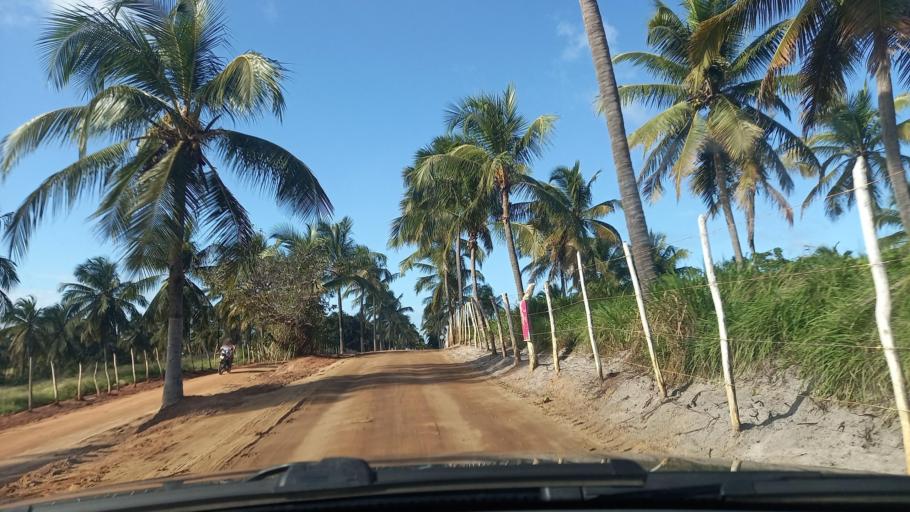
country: BR
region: Alagoas
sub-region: Marechal Deodoro
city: Marechal Deodoro
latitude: -9.8622
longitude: -35.9118
